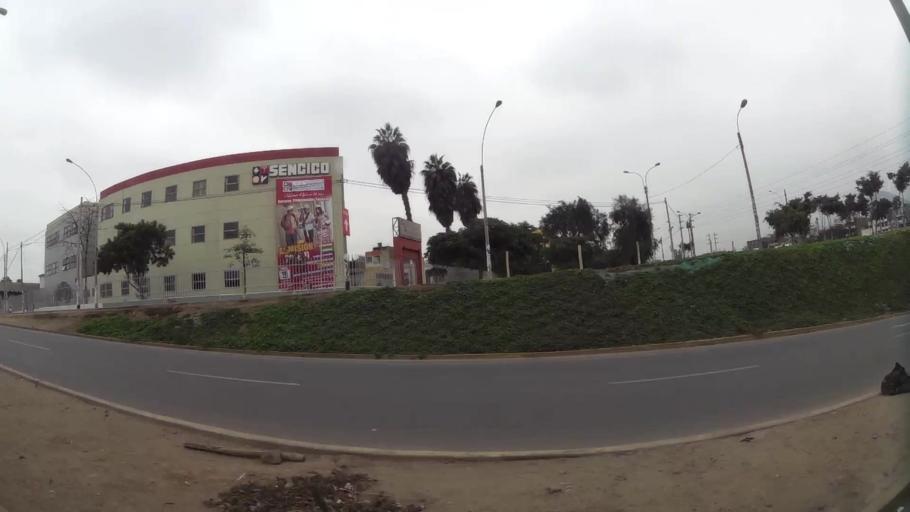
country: PE
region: Lima
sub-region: Lima
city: Independencia
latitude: -11.9843
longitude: -77.0657
